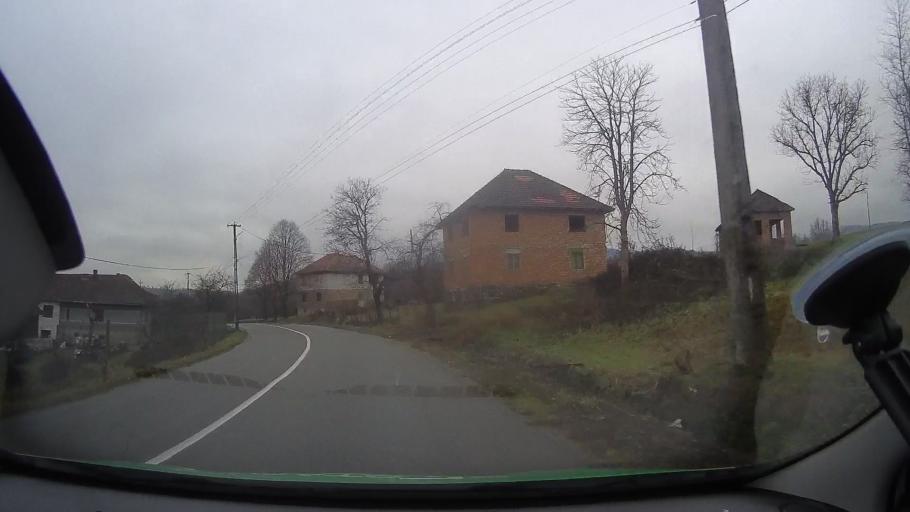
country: RO
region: Arad
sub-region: Comuna Varfurile
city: Varfurile
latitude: 46.3145
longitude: 22.5124
